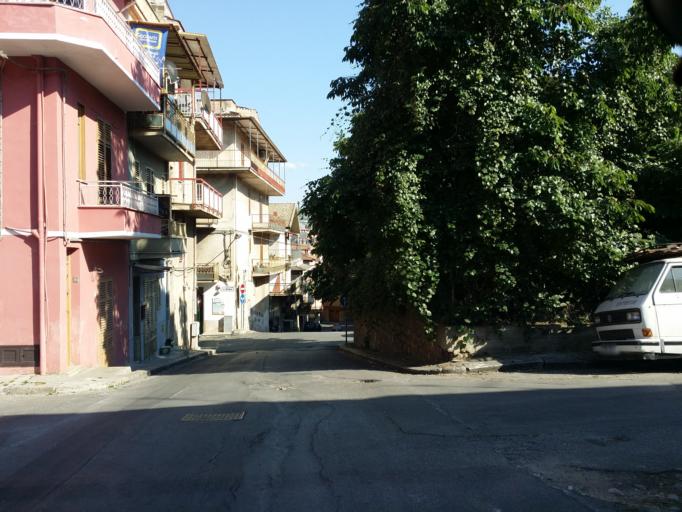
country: IT
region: Sicily
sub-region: Palermo
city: Misilmeri
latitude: 38.0312
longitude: 13.4459
